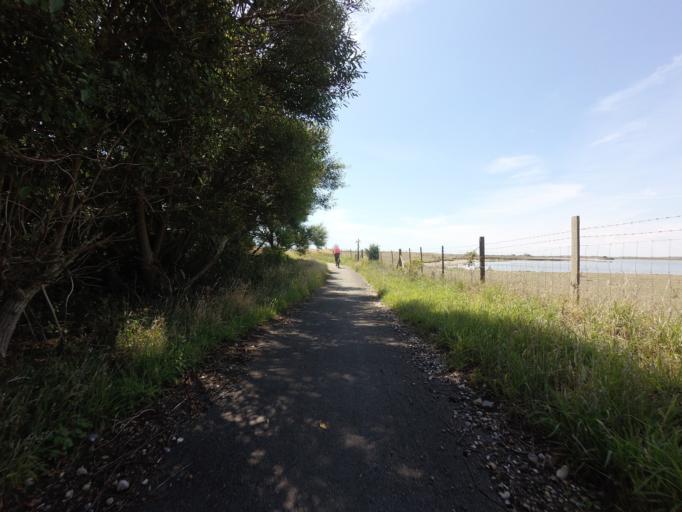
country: GB
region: England
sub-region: Kent
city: Lydd
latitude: 50.9357
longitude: 0.8639
